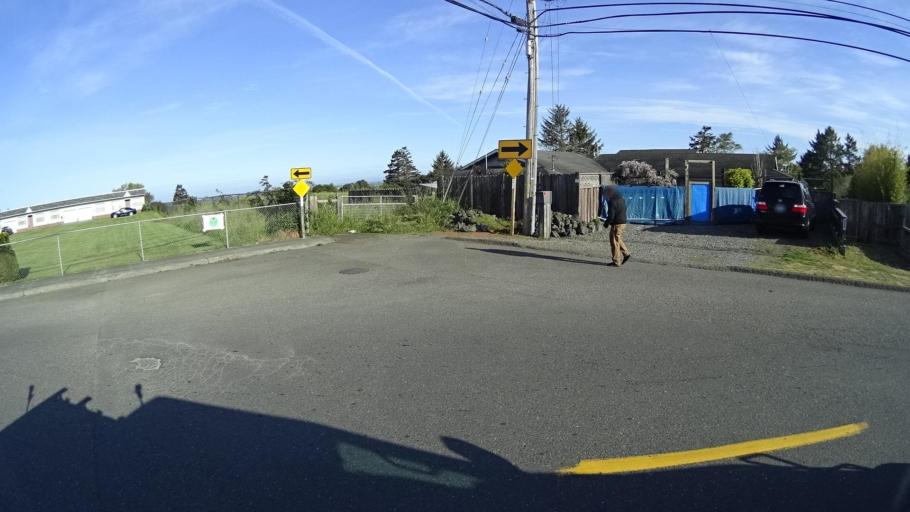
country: US
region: California
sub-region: Humboldt County
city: Bayview
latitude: 40.7608
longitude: -124.1810
